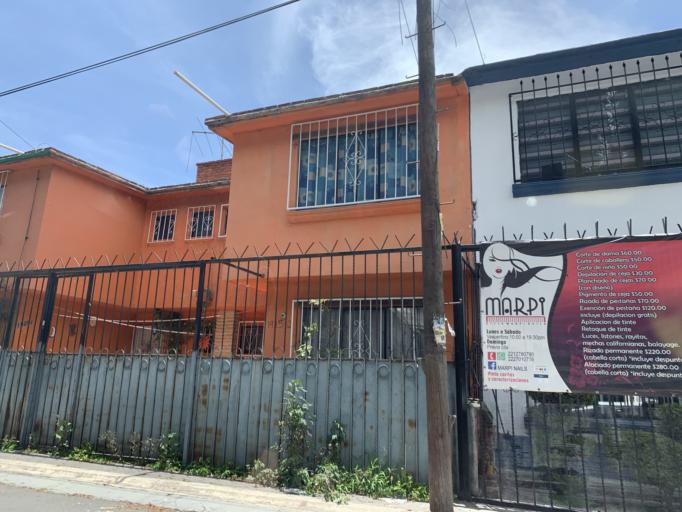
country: MX
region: Puebla
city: Puebla
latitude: 19.0696
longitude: -98.2023
